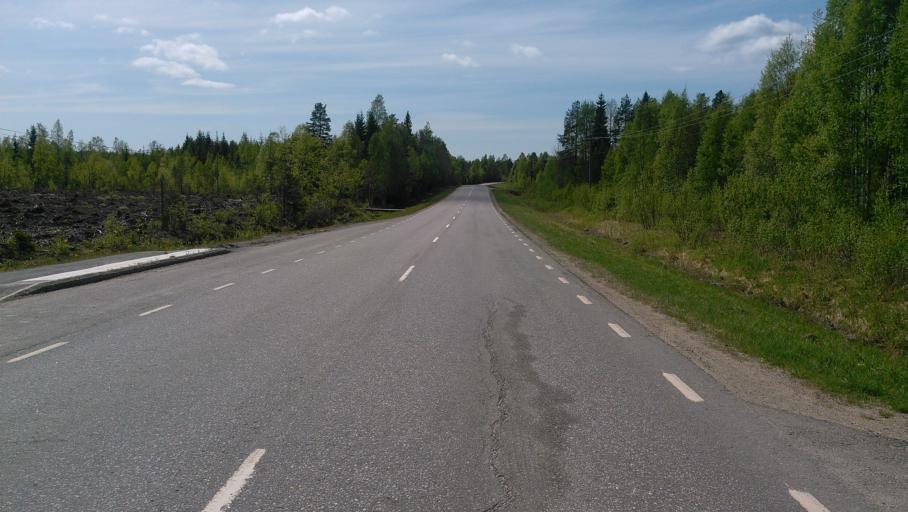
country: SE
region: Vaesterbotten
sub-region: Vannas Kommun
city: Vannasby
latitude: 63.8562
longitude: 19.9982
